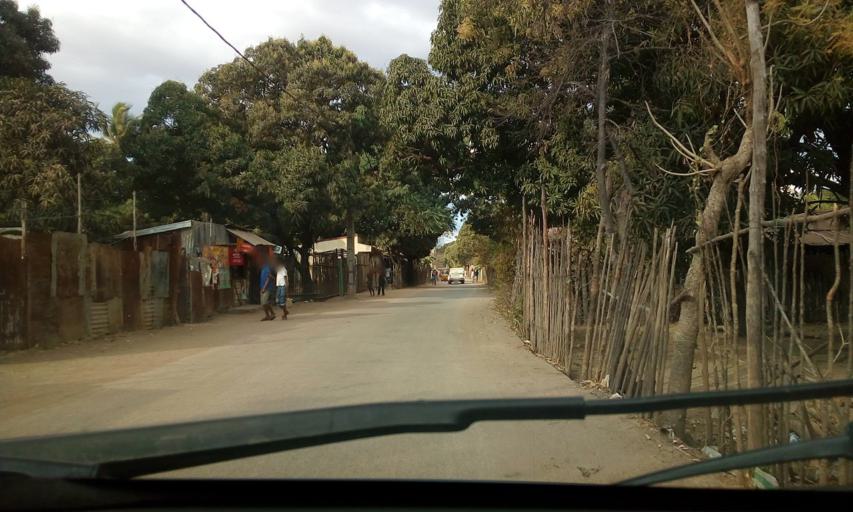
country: MG
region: Boeny
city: Mahajanga
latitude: -15.7061
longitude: 46.3328
